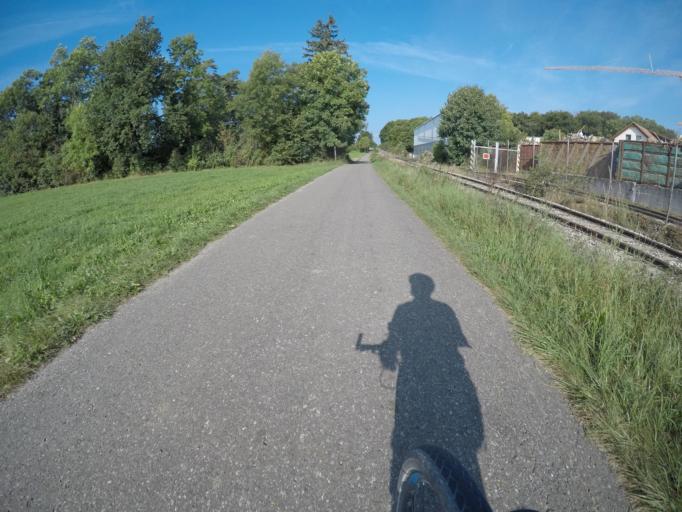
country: DE
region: Baden-Wuerttemberg
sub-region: Regierungsbezirk Stuttgart
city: Gerstetten
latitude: 48.6315
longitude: 9.9821
